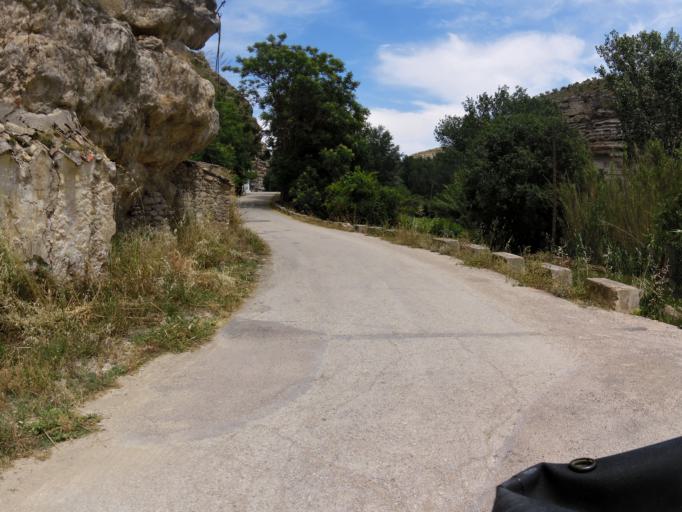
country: ES
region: Castille-La Mancha
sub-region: Provincia de Albacete
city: Casas de Juan Nunez
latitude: 39.1571
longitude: -1.5736
